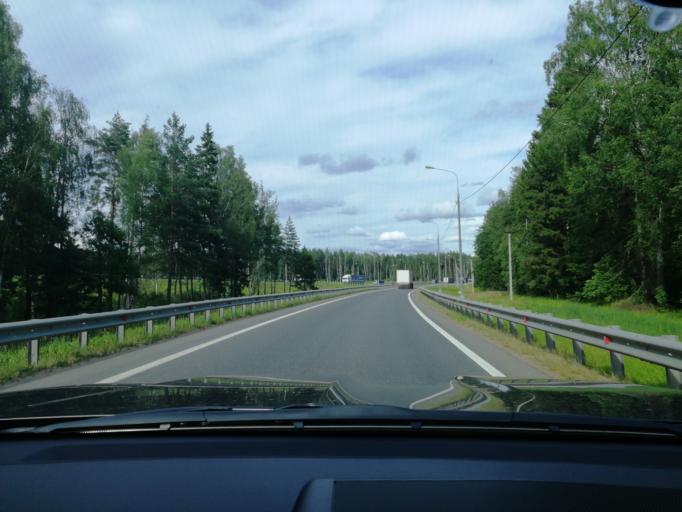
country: RU
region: Moskovskaya
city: Novyy Byt
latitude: 55.0361
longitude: 37.5636
